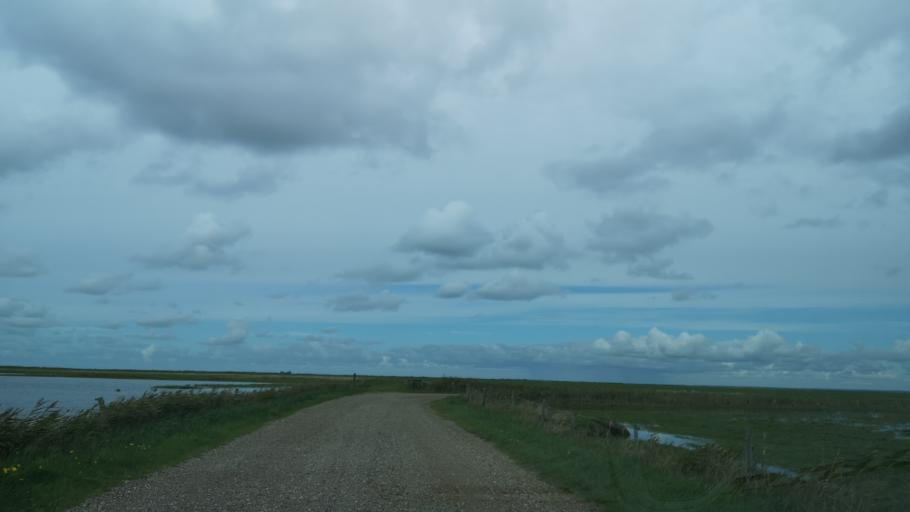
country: DK
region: Central Jutland
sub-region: Ringkobing-Skjern Kommune
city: Hvide Sande
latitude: 55.8666
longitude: 8.2204
